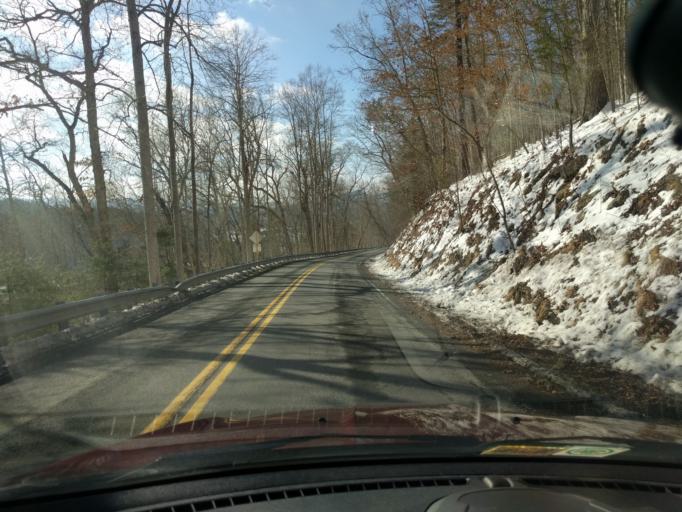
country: US
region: Virginia
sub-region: Bath County
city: Warm Springs
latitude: 38.0852
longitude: -79.8417
